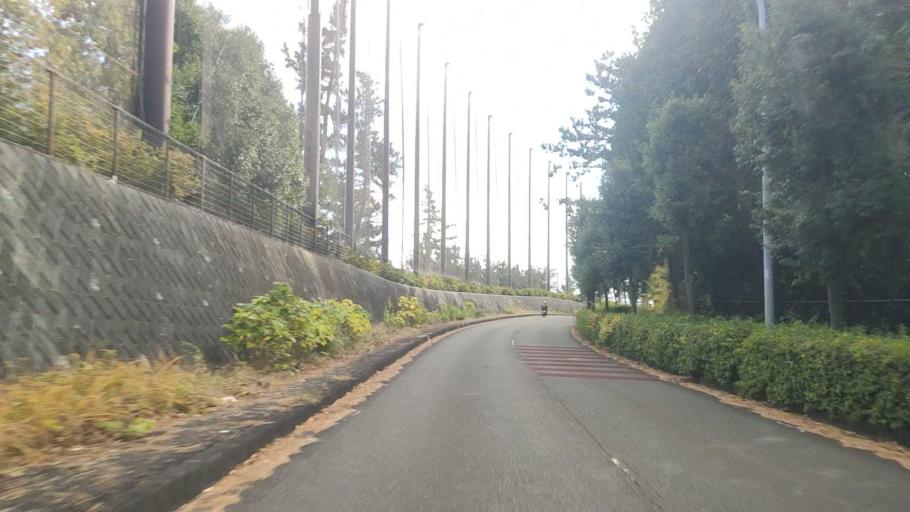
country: JP
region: Kanagawa
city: Yokohama
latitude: 35.4452
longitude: 139.5507
